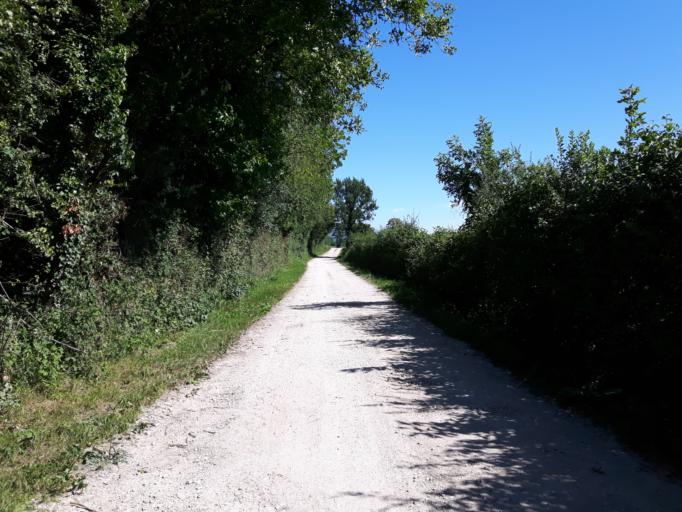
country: FR
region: Franche-Comte
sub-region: Departement du Jura
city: Mouchard
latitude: 47.0176
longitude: 5.8505
